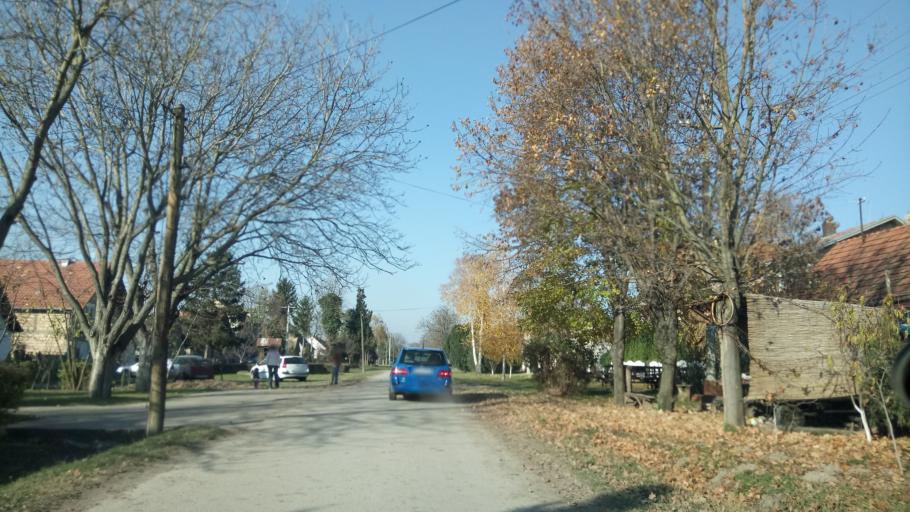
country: RS
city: Ljukovo
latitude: 45.0532
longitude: 20.0262
